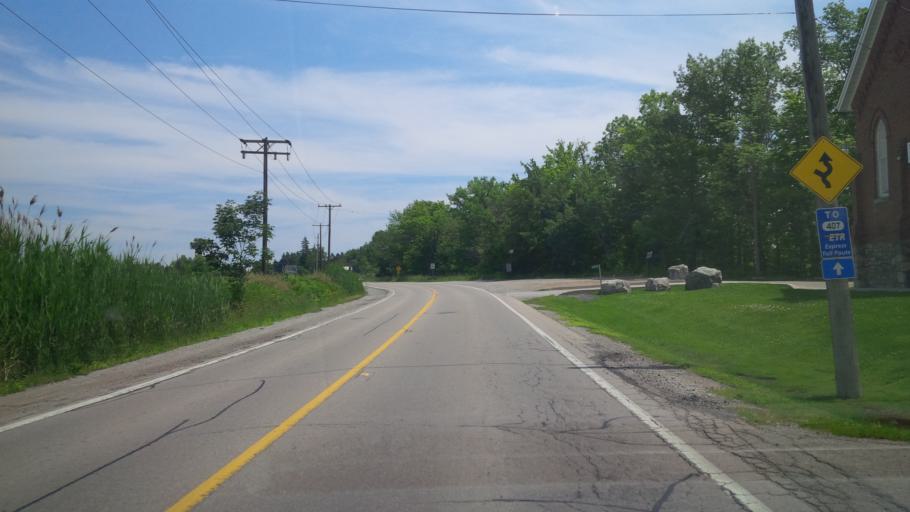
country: CA
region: Ontario
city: Burlington
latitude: 43.4294
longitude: -79.8391
